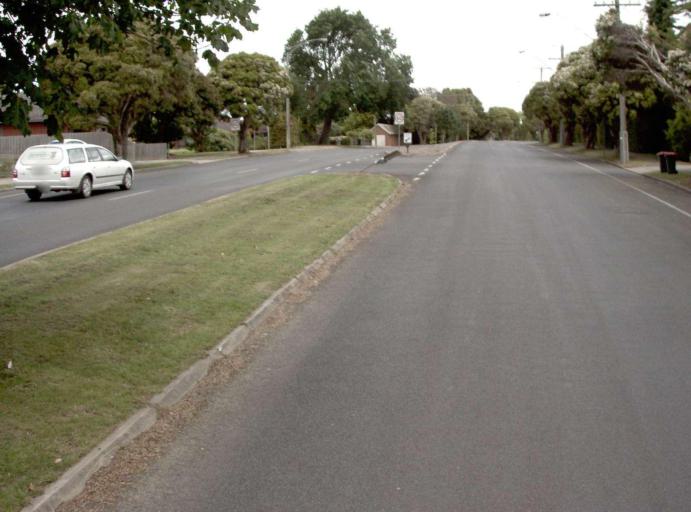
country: AU
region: Victoria
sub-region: Baw Baw
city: Warragul
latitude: -38.1527
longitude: 145.9350
